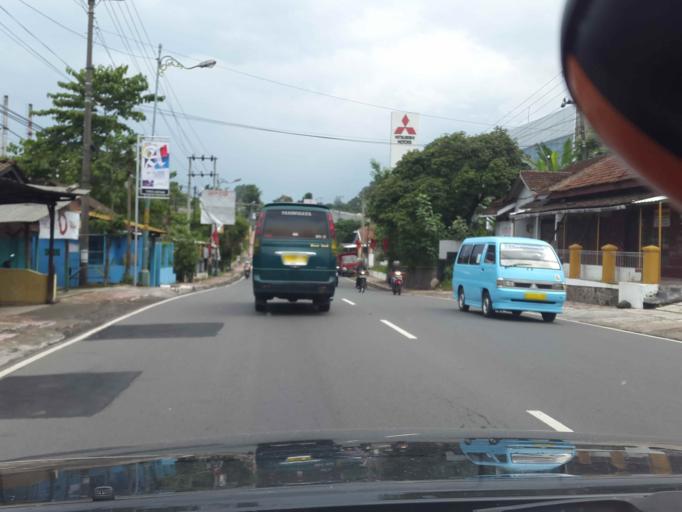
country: ID
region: Central Java
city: Salatiga
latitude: -7.3463
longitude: 110.5117
